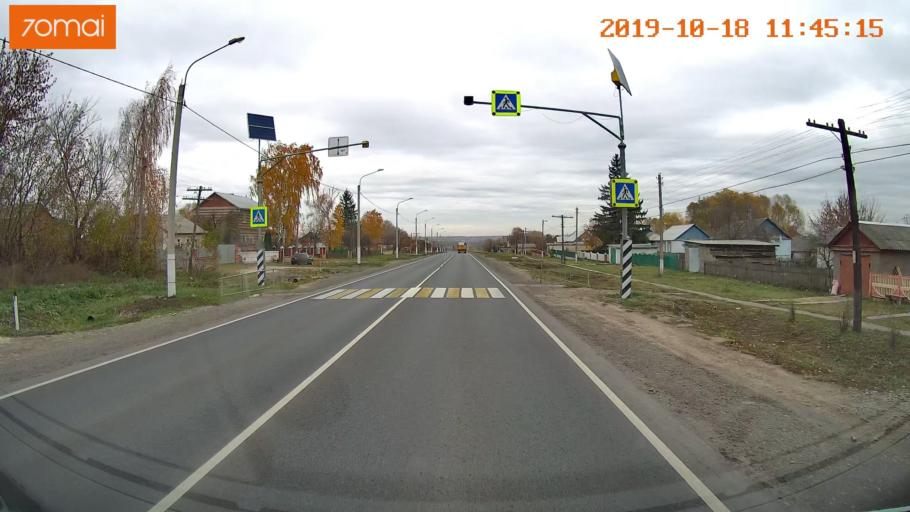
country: RU
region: Rjazan
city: Mikhaylov
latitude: 54.2090
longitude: 38.9679
